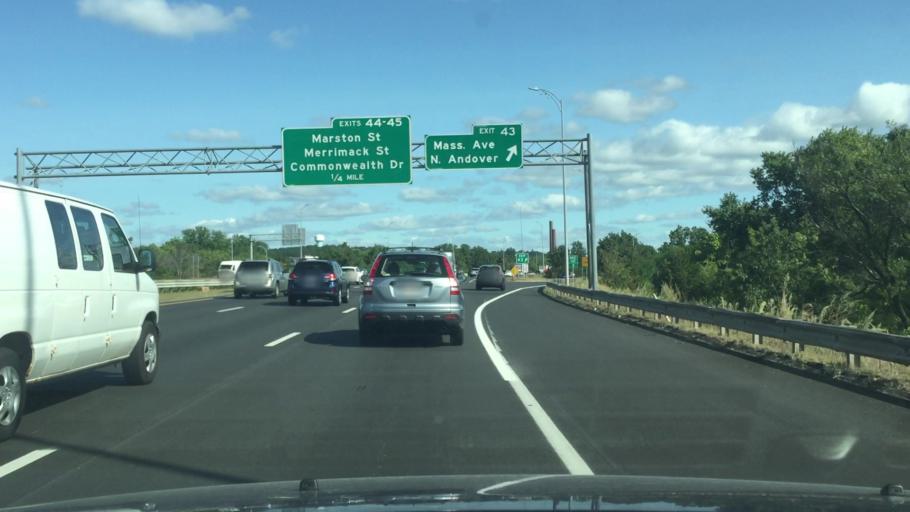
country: US
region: Massachusetts
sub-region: Essex County
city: North Andover
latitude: 42.6945
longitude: -71.1421
